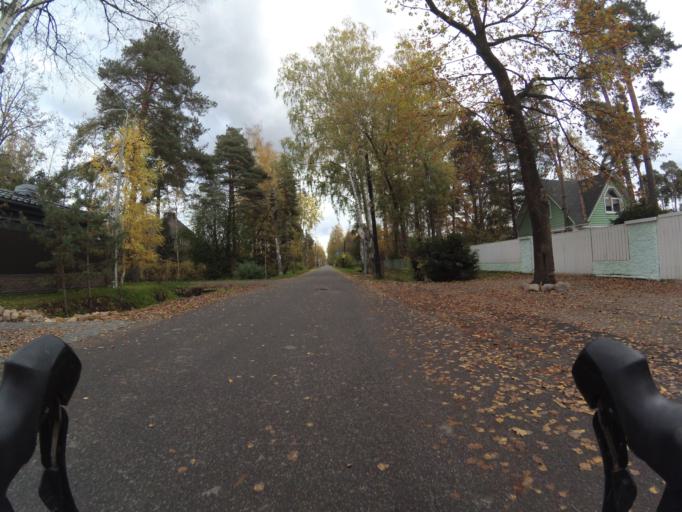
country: RU
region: St.-Petersburg
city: Lakhtinskiy
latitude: 59.9995
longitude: 30.1336
